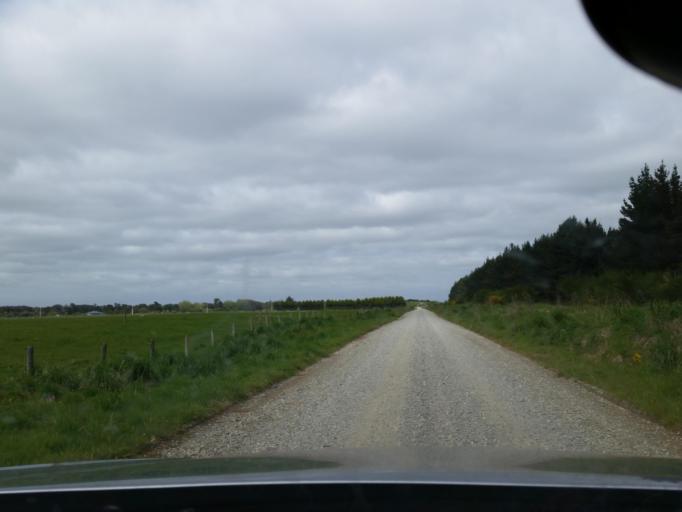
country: NZ
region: Southland
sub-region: Southland District
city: Winton
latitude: -46.2339
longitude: 168.4839
